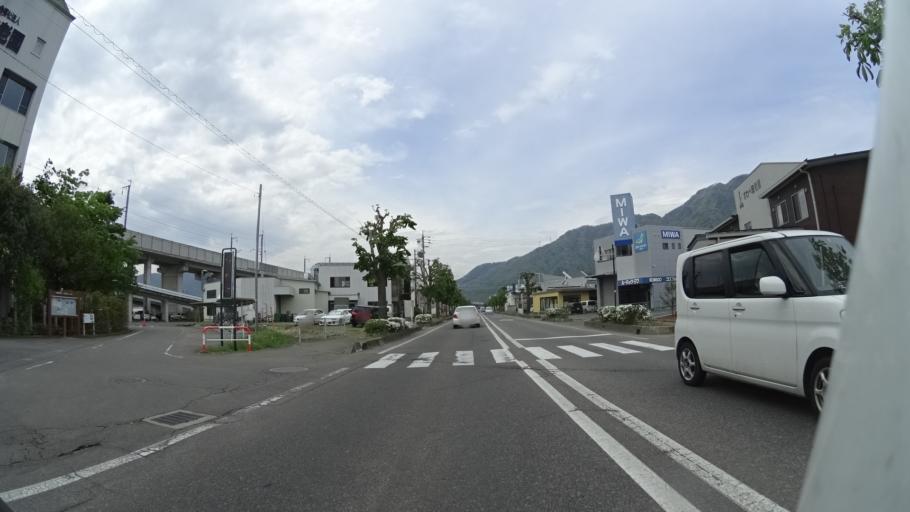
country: JP
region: Nagano
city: Ueda
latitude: 36.4080
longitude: 138.2326
